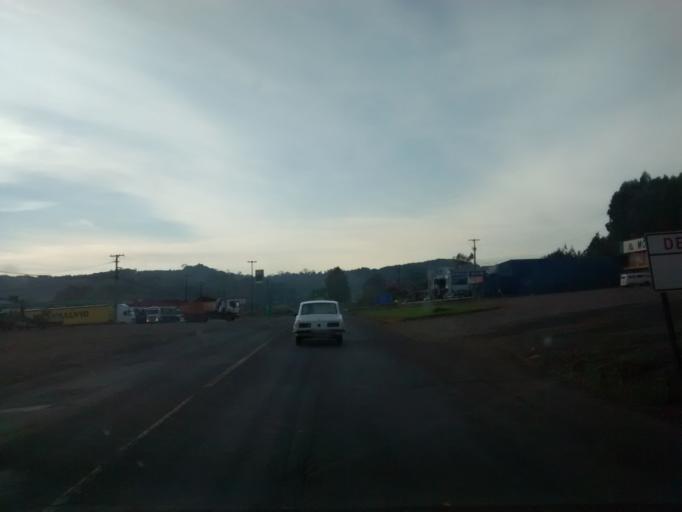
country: BR
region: Parana
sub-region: Francisco Beltrao
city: Francisco Beltrao
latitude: -26.1126
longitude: -53.0471
